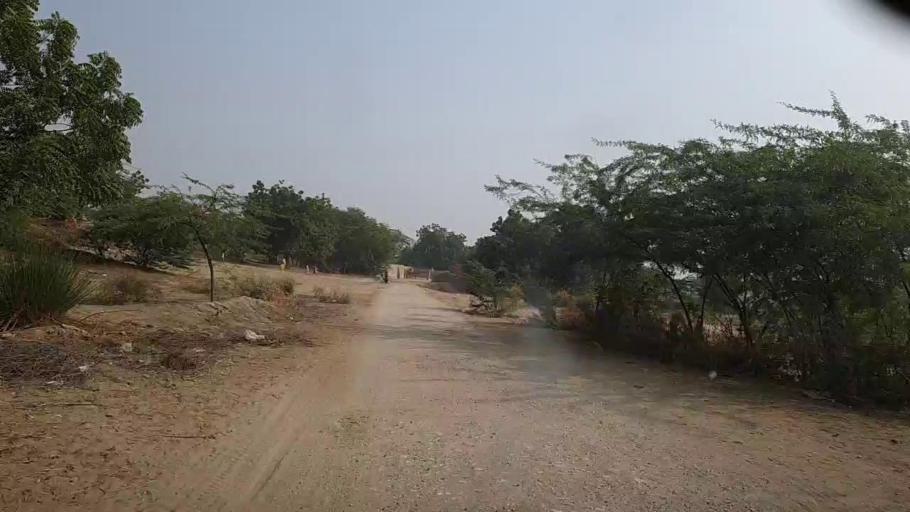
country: PK
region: Sindh
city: Bozdar
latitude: 27.0595
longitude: 68.6518
